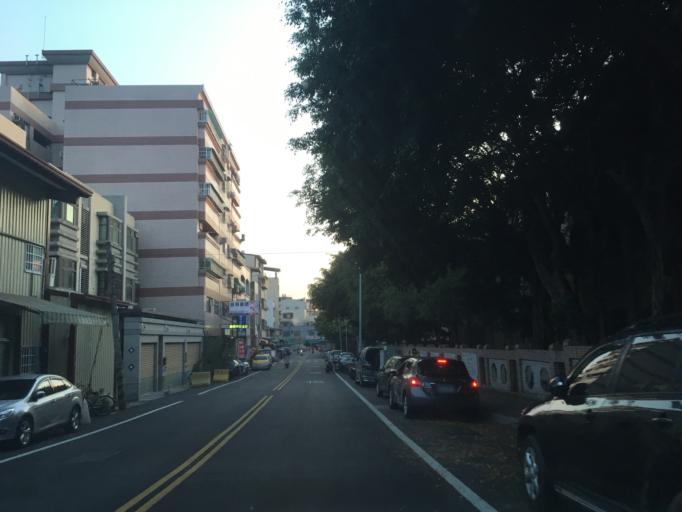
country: TW
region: Taiwan
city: Zhongxing New Village
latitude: 23.9813
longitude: 120.6875
